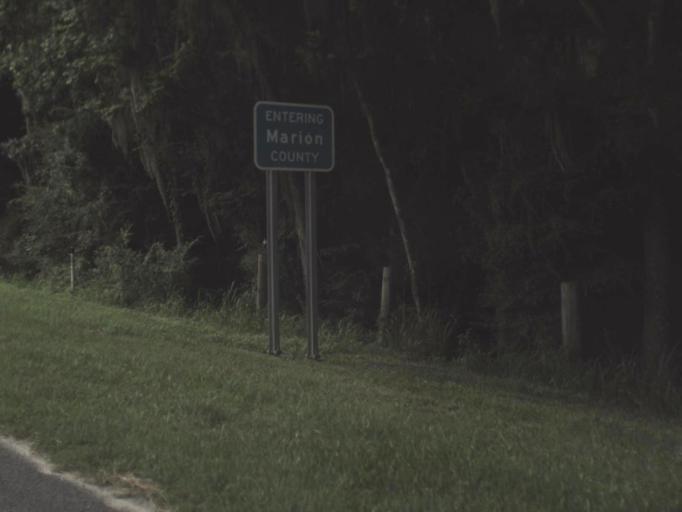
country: US
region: Florida
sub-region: Marion County
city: Citra
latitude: 29.4840
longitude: -82.2439
